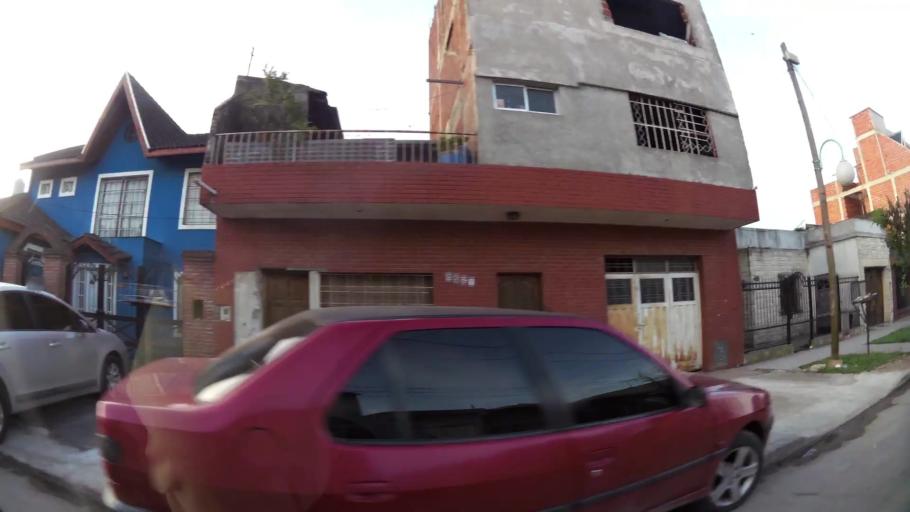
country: AR
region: Buenos Aires
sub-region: Partido de Almirante Brown
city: Adrogue
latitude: -34.7851
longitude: -58.3174
